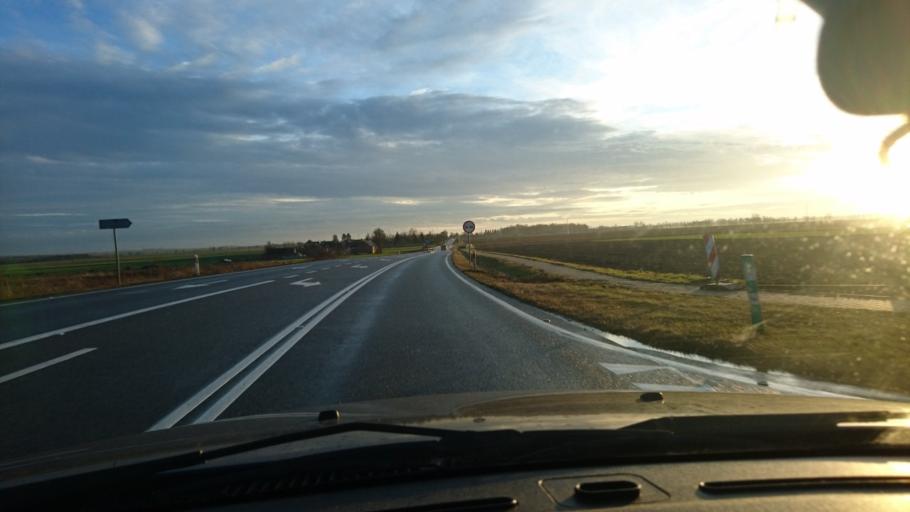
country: PL
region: Greater Poland Voivodeship
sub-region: Powiat kepinski
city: Opatow
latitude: 51.1948
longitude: 18.1484
